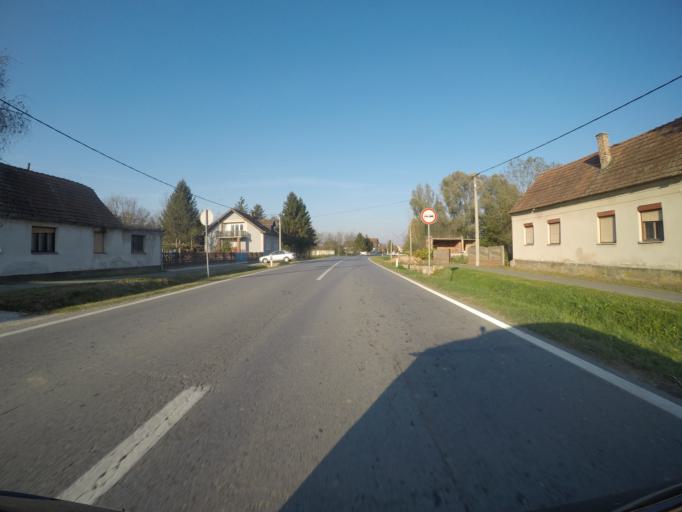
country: HU
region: Somogy
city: Barcs
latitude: 45.8995
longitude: 17.4364
